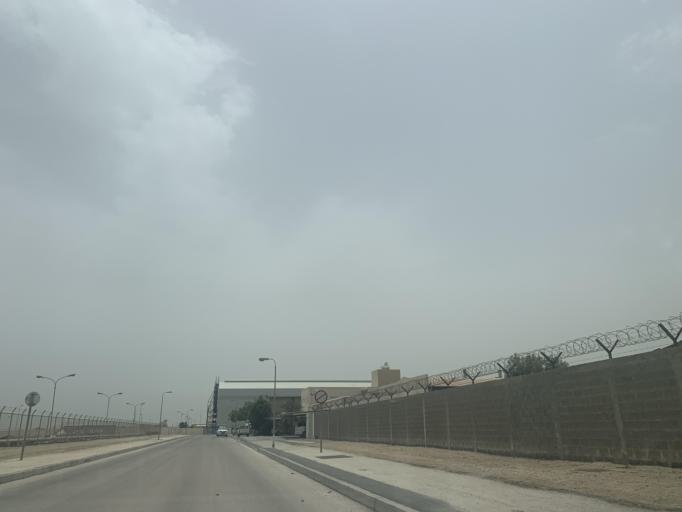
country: BH
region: Northern
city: Sitrah
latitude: 26.1809
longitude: 50.6127
